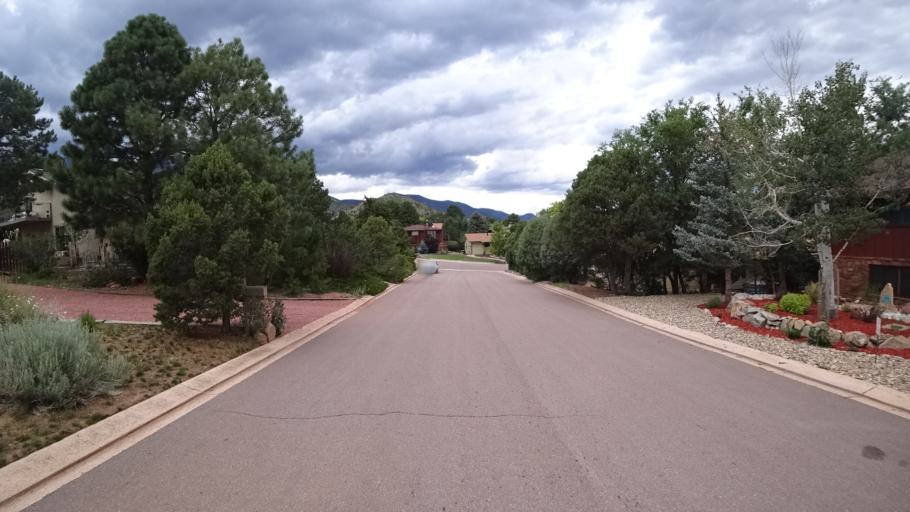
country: US
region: Colorado
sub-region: El Paso County
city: Manitou Springs
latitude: 38.8430
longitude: -104.8956
